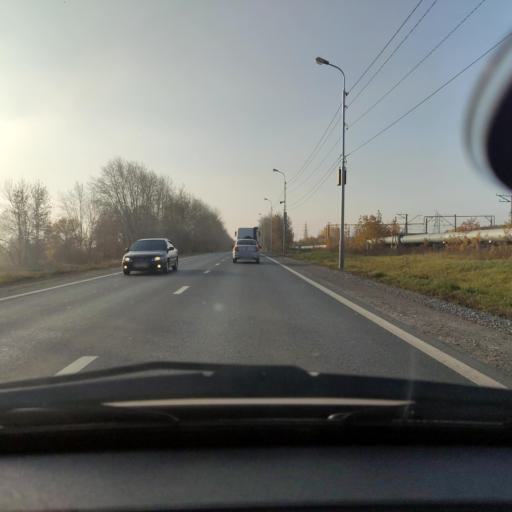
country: RU
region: Bashkortostan
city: Ufa
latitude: 54.8577
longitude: 56.1144
